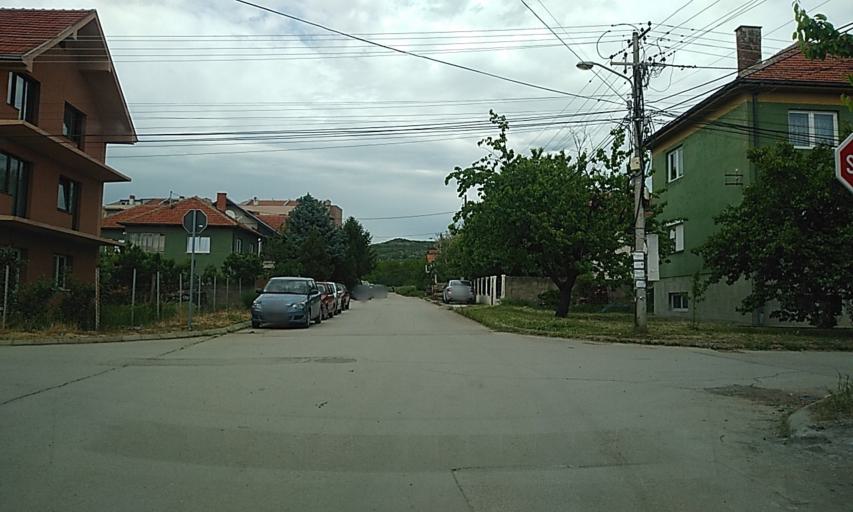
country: RS
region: Central Serbia
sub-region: Nisavski Okrug
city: Nis
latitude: 43.3354
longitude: 21.9057
